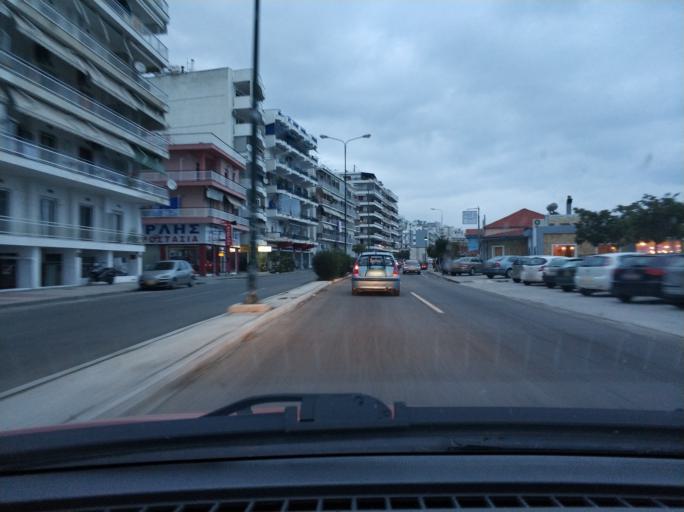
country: GR
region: East Macedonia and Thrace
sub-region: Nomos Kavalas
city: Kavala
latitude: 40.9346
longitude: 24.3950
